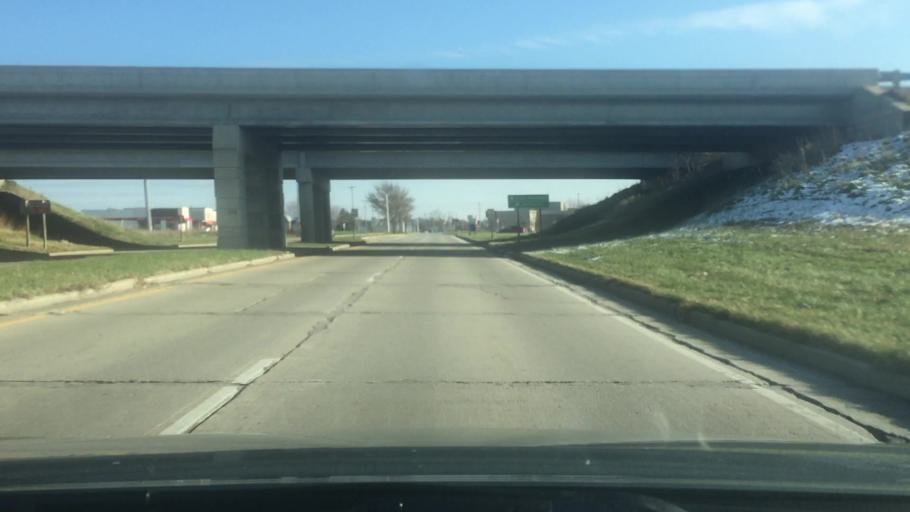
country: US
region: Wisconsin
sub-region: Jefferson County
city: Fort Atkinson
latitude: 42.9439
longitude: -88.8666
